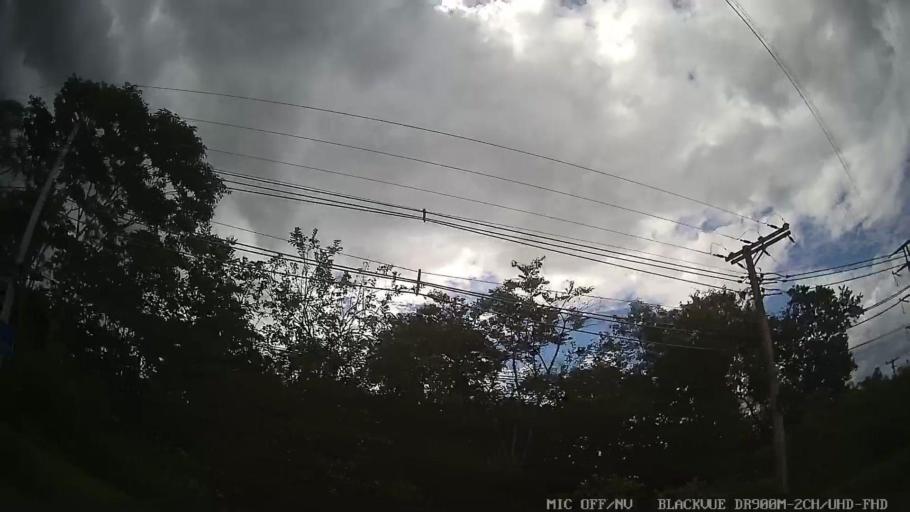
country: BR
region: Sao Paulo
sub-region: Jaguariuna
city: Jaguariuna
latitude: -22.7025
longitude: -46.9996
